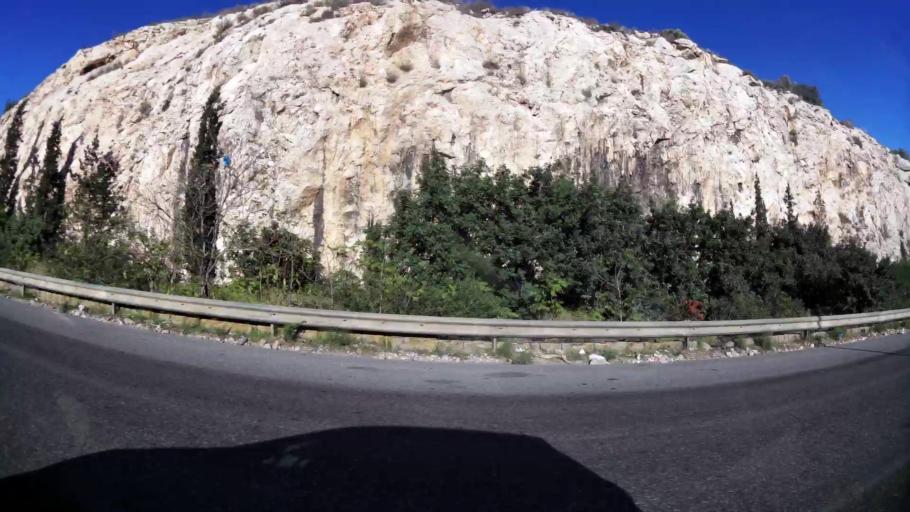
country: GR
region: Attica
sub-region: Nomos Piraios
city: Keratsini
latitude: 37.9769
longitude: 23.5989
